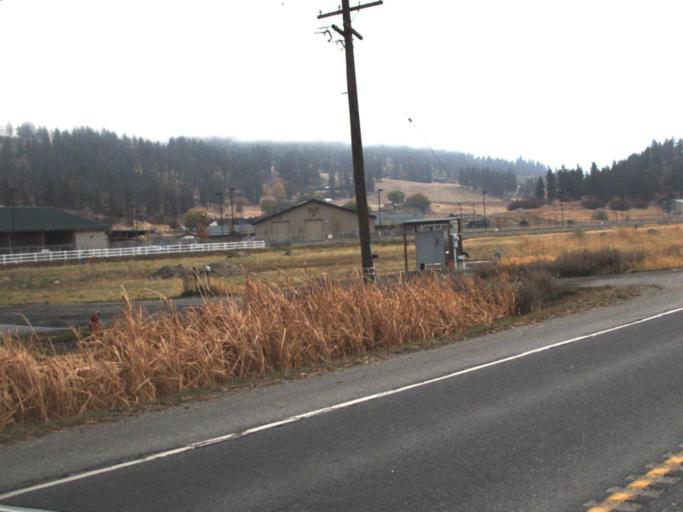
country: US
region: Washington
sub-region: Stevens County
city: Colville
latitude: 48.5613
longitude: -117.9302
